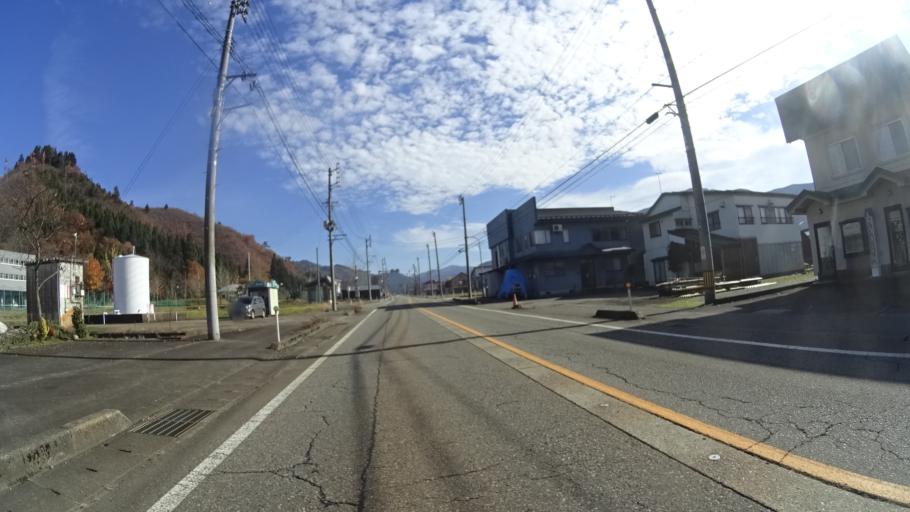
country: JP
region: Niigata
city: Muikamachi
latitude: 37.2287
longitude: 138.9857
